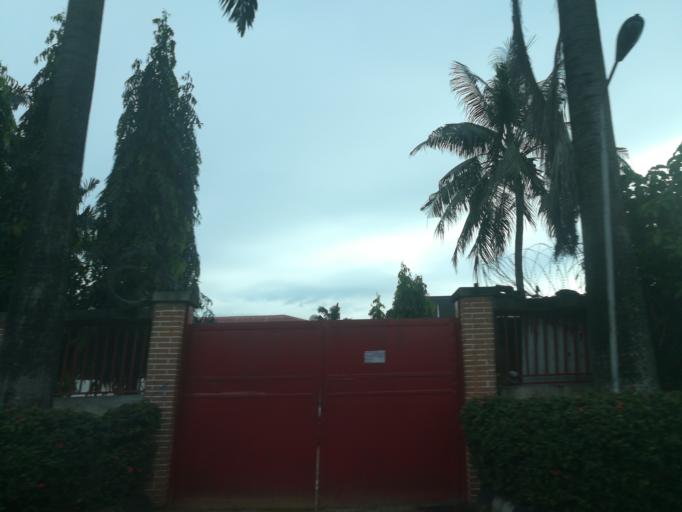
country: NG
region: Rivers
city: Port Harcourt
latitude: 4.8129
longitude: 7.0010
